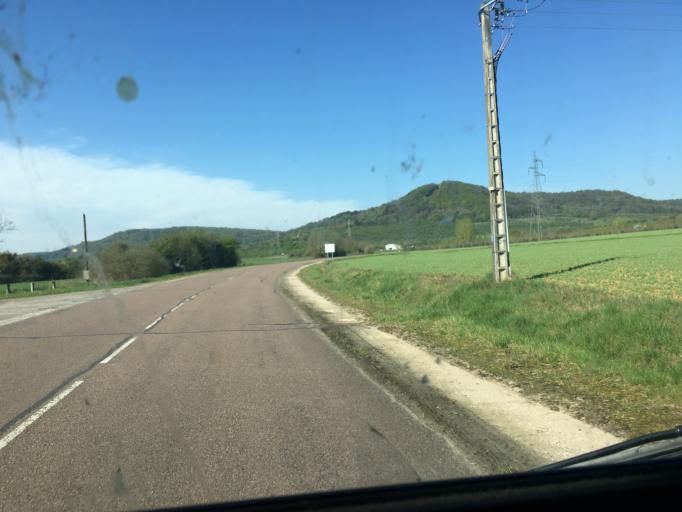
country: FR
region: Lorraine
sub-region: Departement de la Meuse
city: Vigneulles-les-Hattonchatel
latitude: 48.9382
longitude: 5.7085
